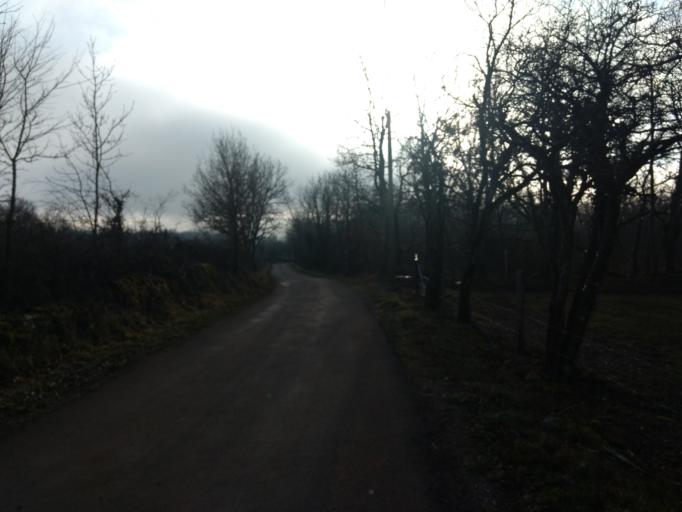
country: FR
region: Midi-Pyrenees
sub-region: Departement de l'Aveyron
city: Salles-la-Source
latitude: 44.4439
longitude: 2.5222
